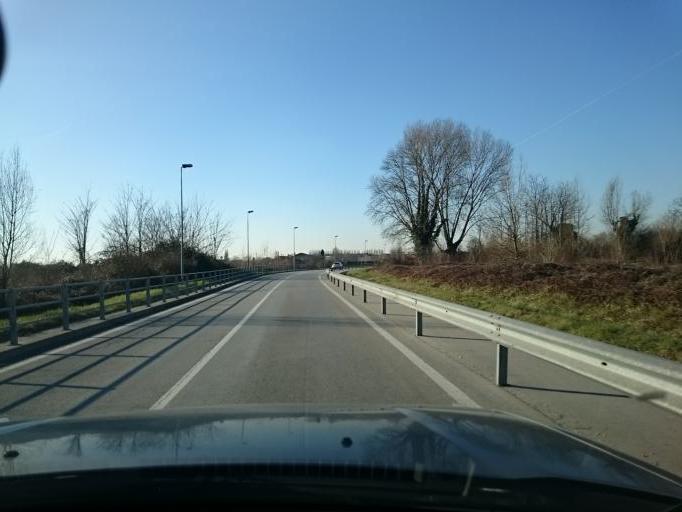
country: IT
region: Veneto
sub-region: Provincia di Venezia
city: Mira Taglio
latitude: 45.4350
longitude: 12.1572
